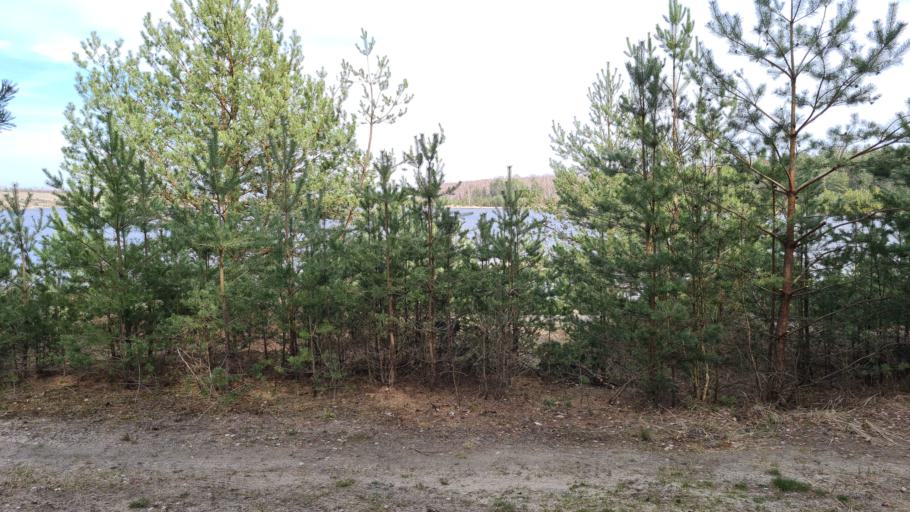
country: DE
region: Brandenburg
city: Lauchhammer
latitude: 51.5409
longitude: 13.7160
